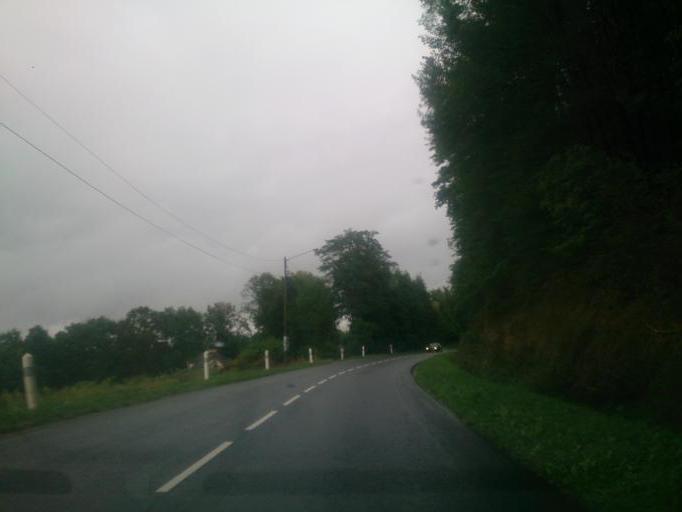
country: FR
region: Limousin
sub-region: Departement de la Correze
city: Malemort-sur-Correze
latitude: 45.1807
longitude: 1.5719
